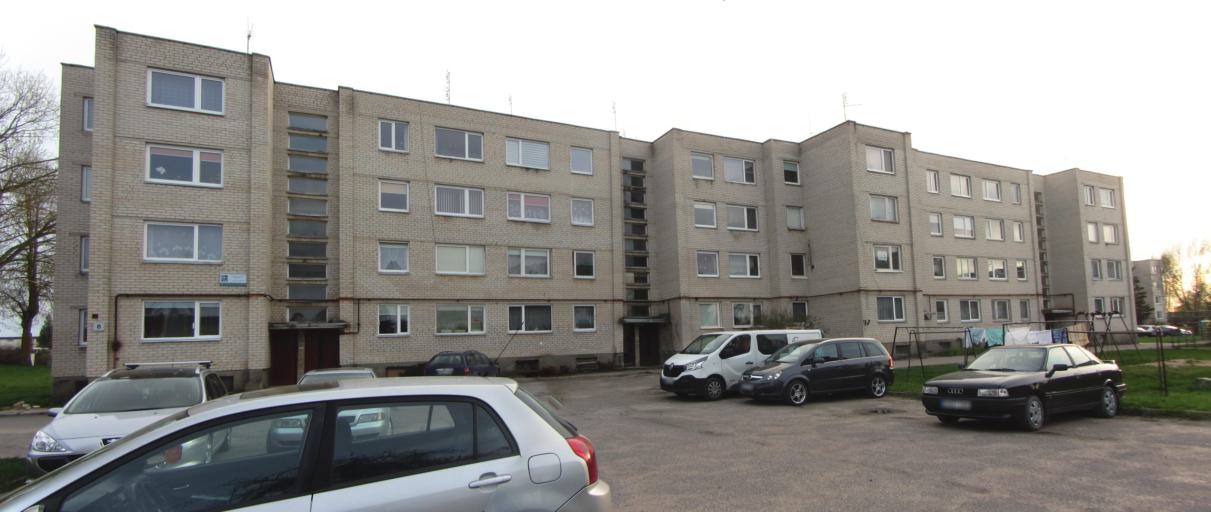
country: LT
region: Utenos apskritis
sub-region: Utena
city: Utena
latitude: 55.7384
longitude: 25.8310
